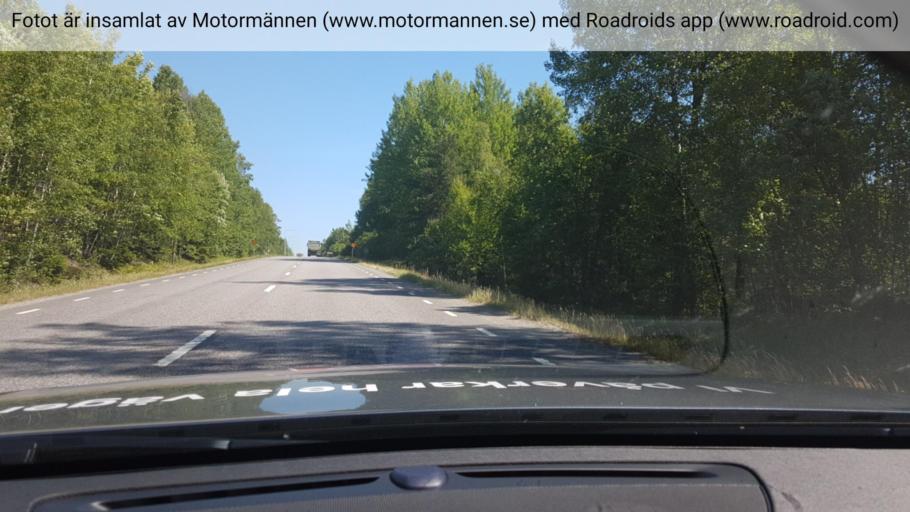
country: SE
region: Stockholm
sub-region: Haninge Kommun
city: Handen
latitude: 59.1945
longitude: 18.1186
